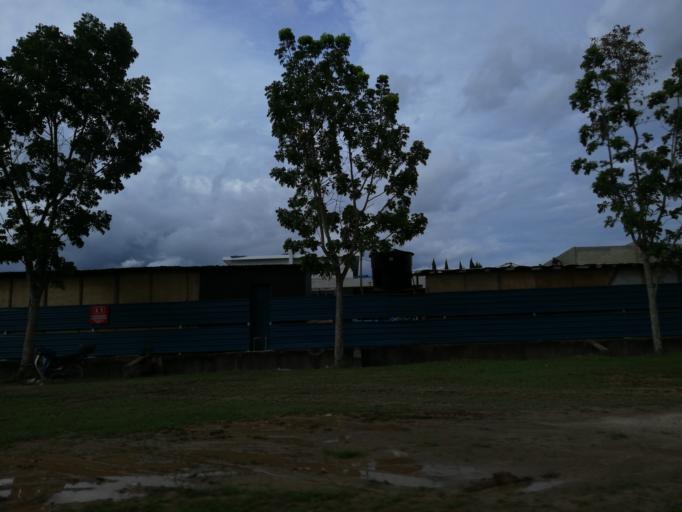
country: MY
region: Penang
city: Tasek Glugor
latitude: 5.4984
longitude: 100.6243
